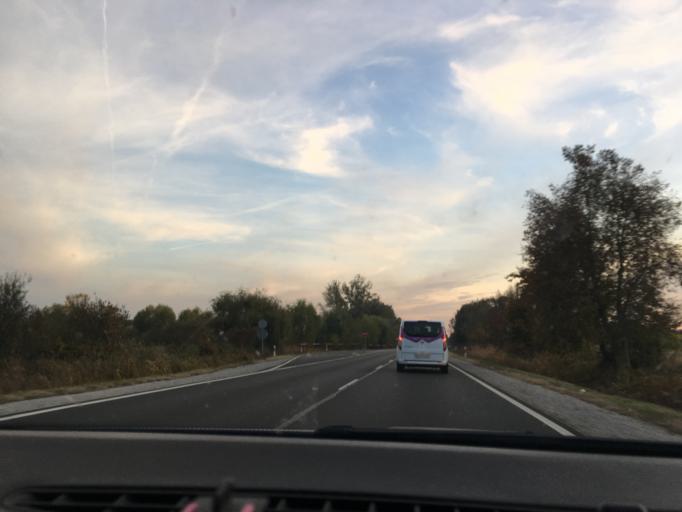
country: HU
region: Hajdu-Bihar
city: Hajduhadhaz
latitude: 47.6951
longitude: 21.6562
